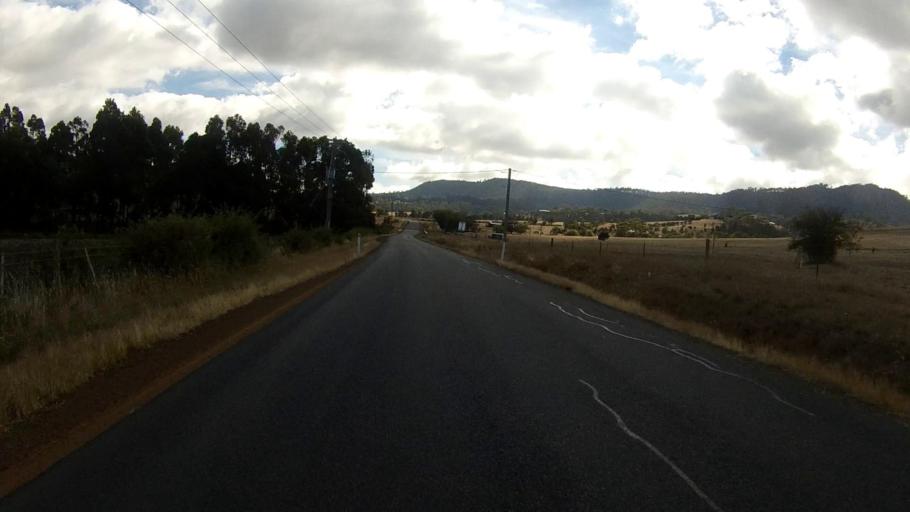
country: AU
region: Tasmania
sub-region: Brighton
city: Old Beach
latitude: -42.7687
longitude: 147.2959
